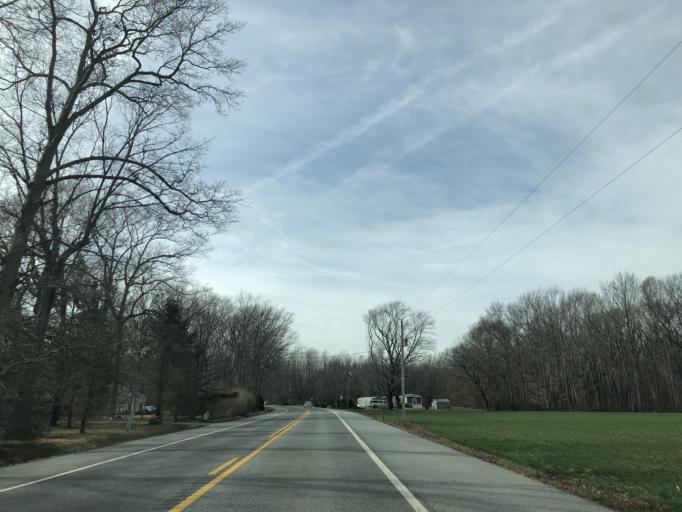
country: US
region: Delaware
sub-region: Kent County
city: Smyrna
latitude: 39.2808
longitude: -75.5558
